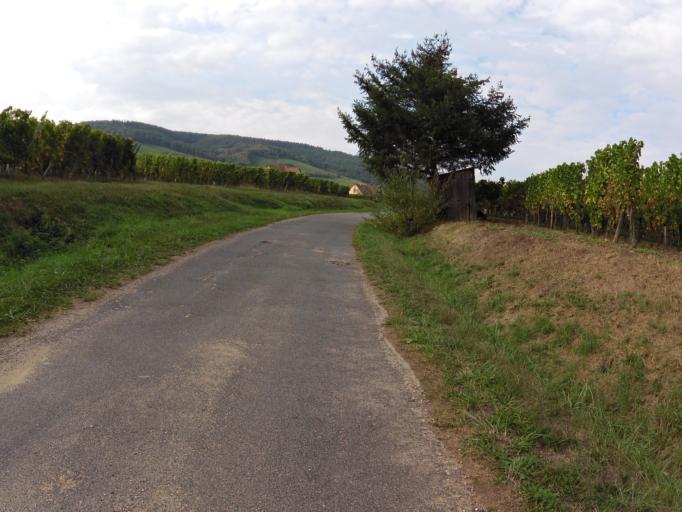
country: FR
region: Alsace
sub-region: Departement du Bas-Rhin
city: Kintzheim
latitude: 48.2391
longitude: 7.3879
